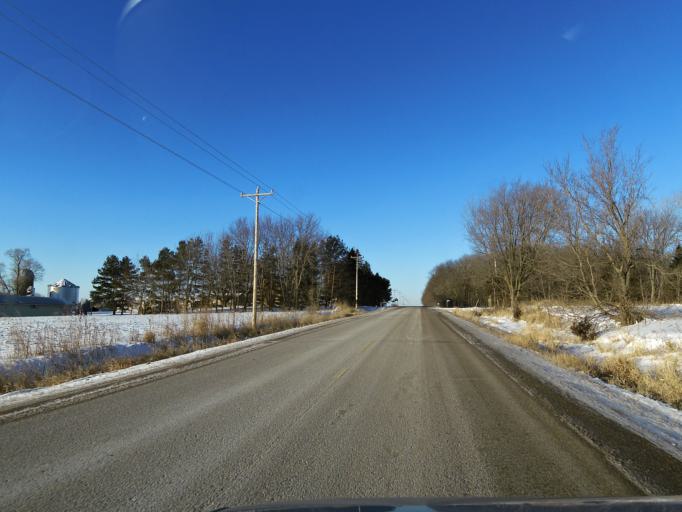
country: US
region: Minnesota
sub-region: Scott County
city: Jordan
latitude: 44.6597
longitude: -93.5641
